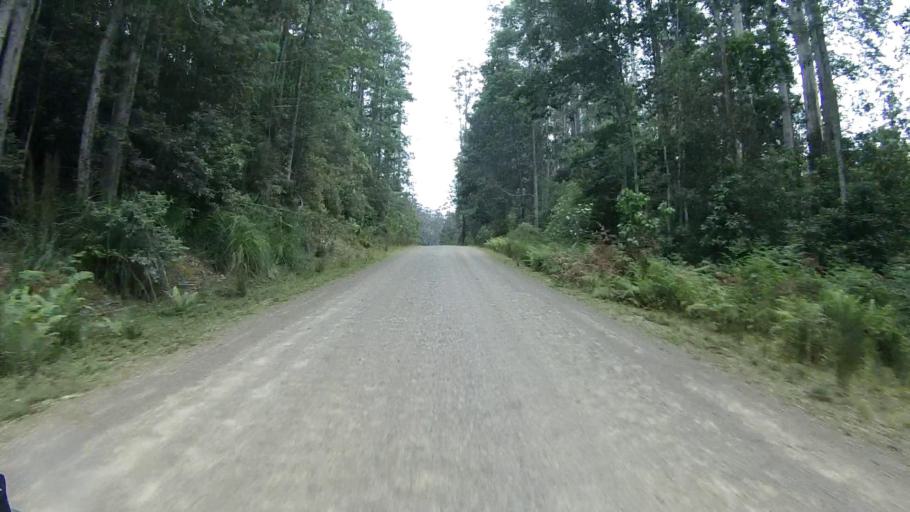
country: AU
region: Tasmania
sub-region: Sorell
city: Sorell
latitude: -42.7154
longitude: 147.8417
